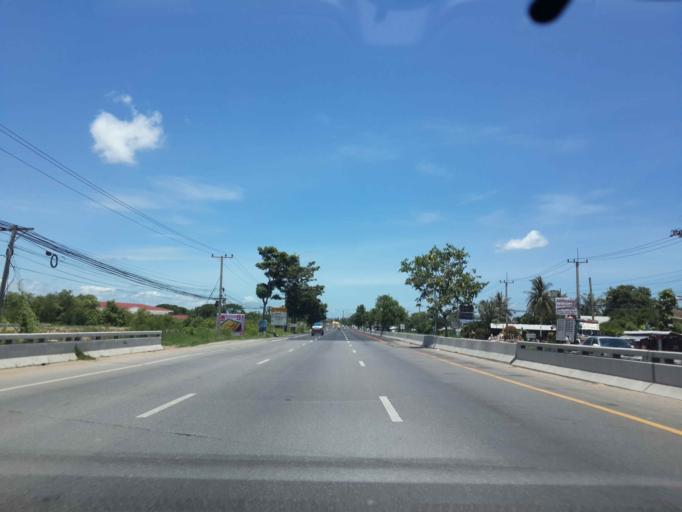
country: TH
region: Phetchaburi
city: Tha Yang
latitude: 12.8716
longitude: 99.9167
